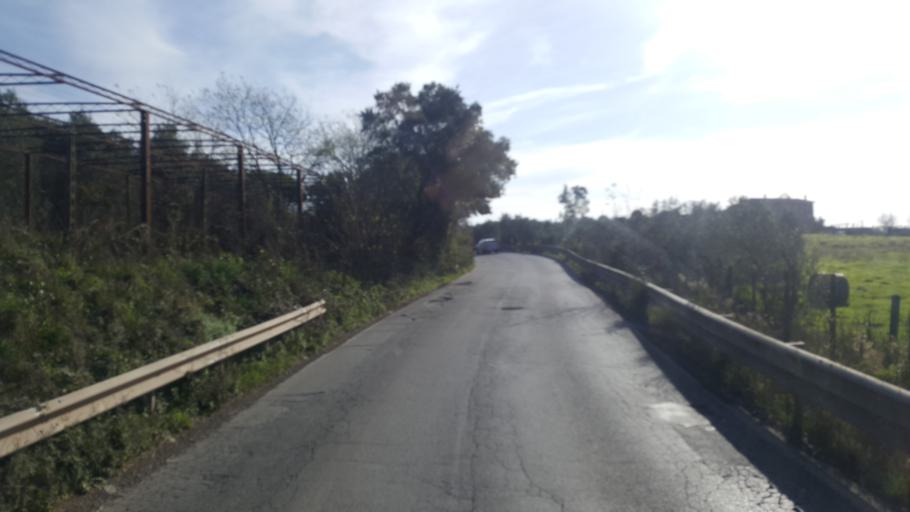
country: IT
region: Latium
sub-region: Citta metropolitana di Roma Capitale
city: Mantiglia di Ardea
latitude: 41.6828
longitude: 12.6173
